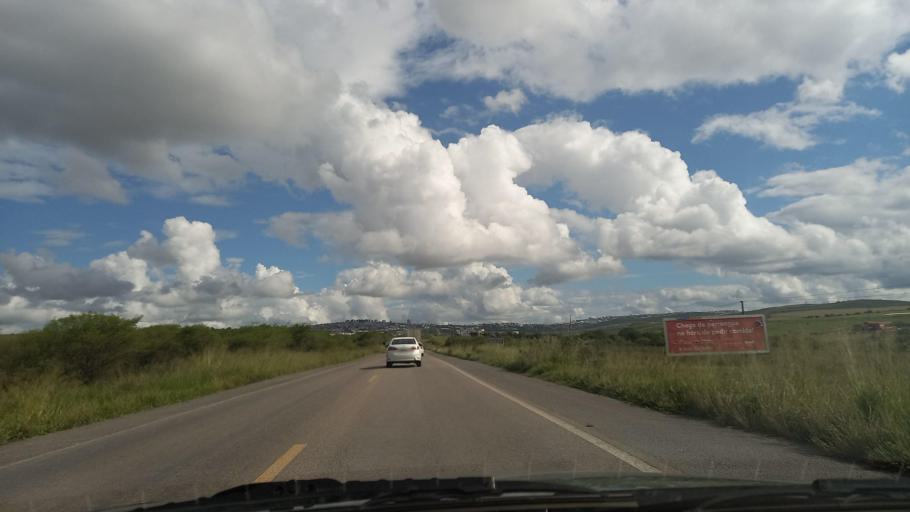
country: BR
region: Pernambuco
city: Garanhuns
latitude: -8.8372
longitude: -36.4556
